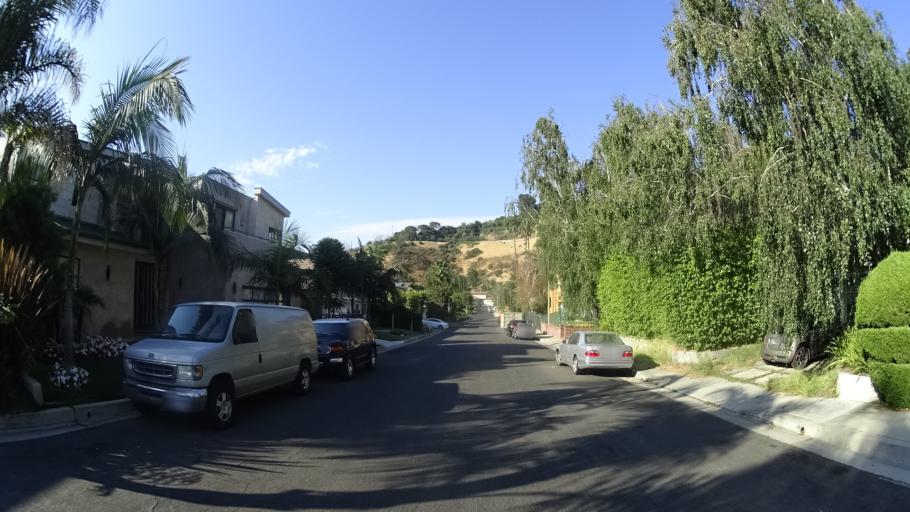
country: US
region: California
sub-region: Los Angeles County
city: Universal City
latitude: 34.1274
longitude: -118.3754
